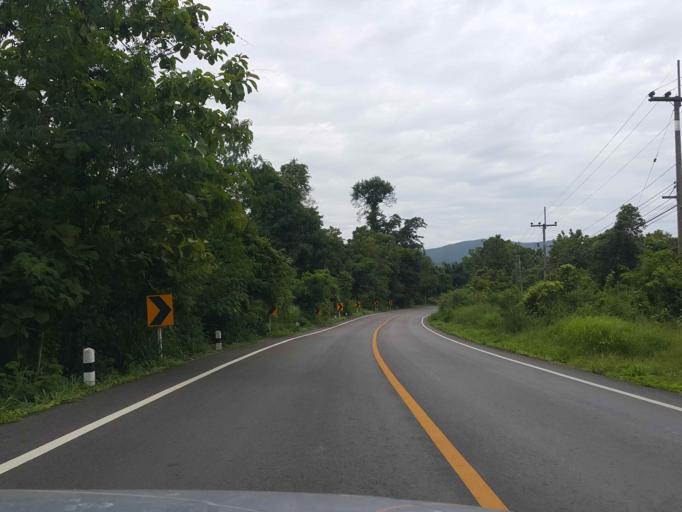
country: TH
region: Lampang
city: Thoen
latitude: 17.5579
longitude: 99.3347
